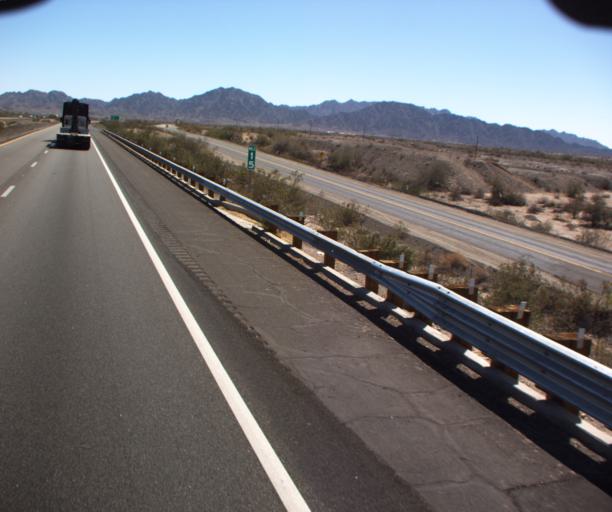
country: US
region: Arizona
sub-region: Yuma County
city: Fortuna Foothills
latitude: 32.6672
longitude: -114.3976
